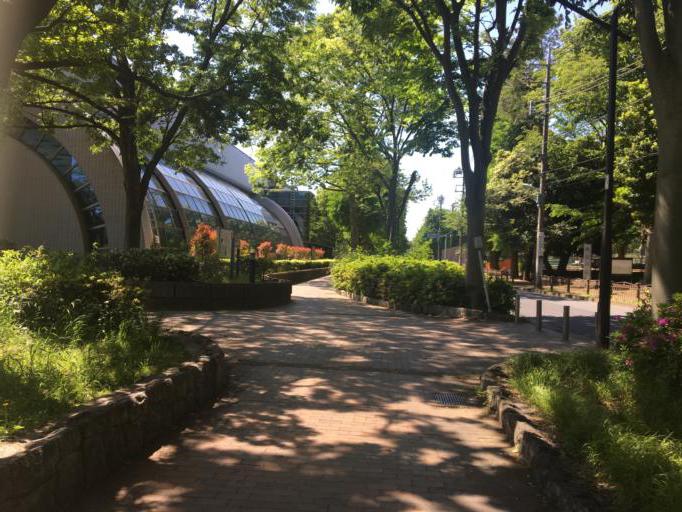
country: JP
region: Saitama
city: Shimotoda
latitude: 35.7579
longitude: 139.6752
